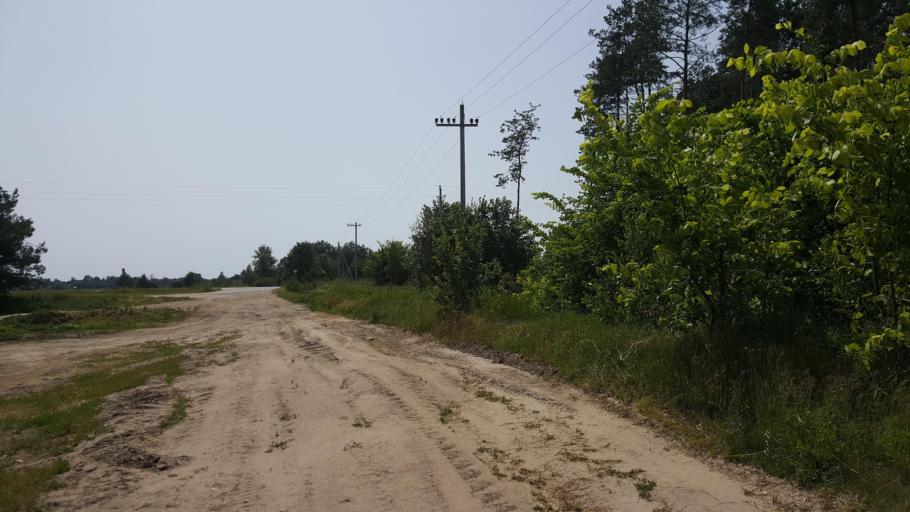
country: BY
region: Brest
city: Kamyanyets
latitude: 52.4688
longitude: 23.8268
